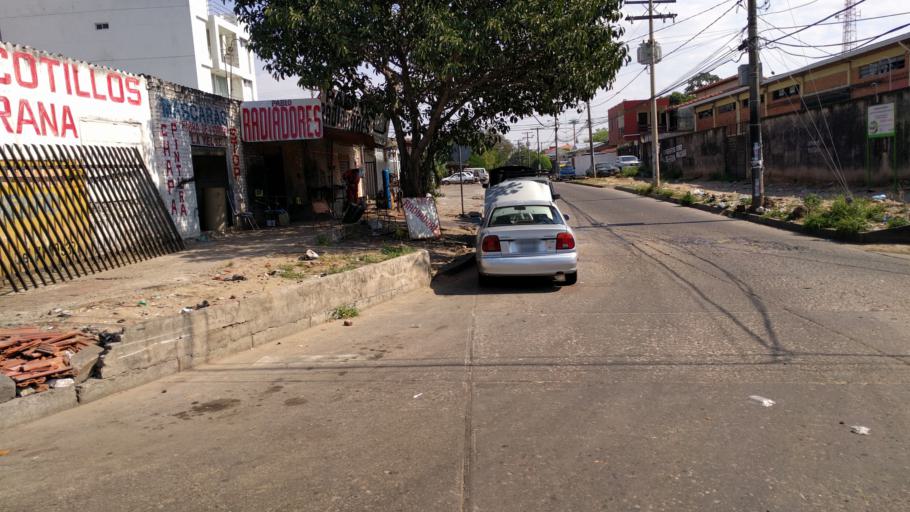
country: BO
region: Santa Cruz
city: Santa Cruz de la Sierra
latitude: -17.8050
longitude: -63.1987
